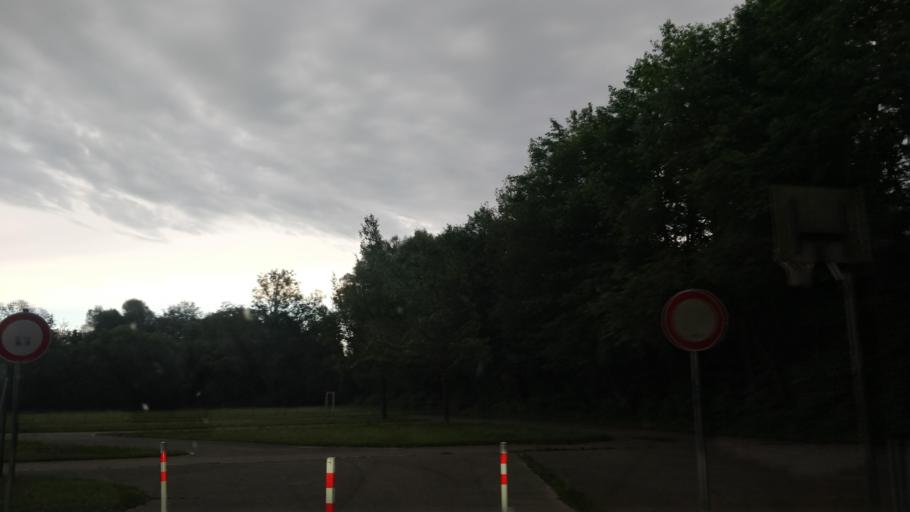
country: DE
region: Bavaria
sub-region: Upper Bavaria
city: Schwindegg
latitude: 48.2698
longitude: 12.2543
